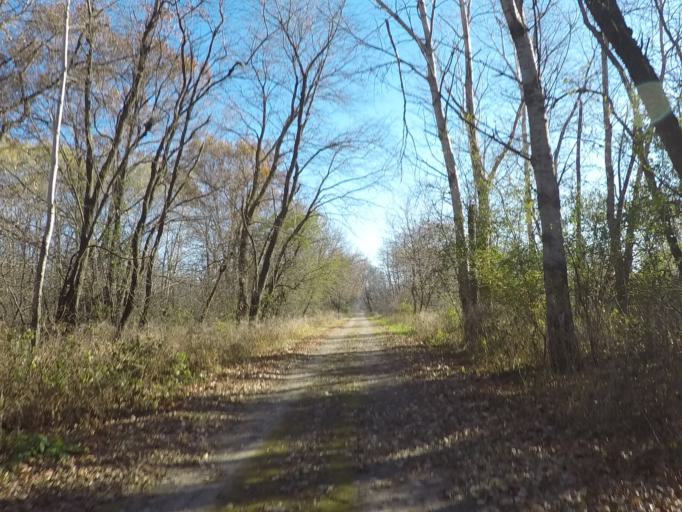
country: US
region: Wisconsin
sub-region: Dane County
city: Deerfield
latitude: 43.0425
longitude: -89.0379
